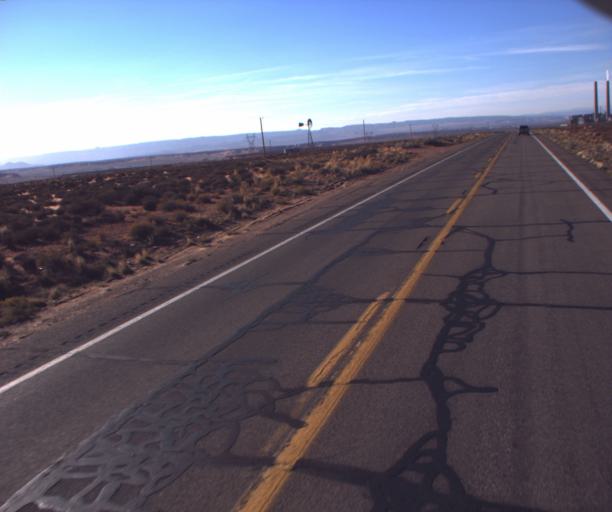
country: US
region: Arizona
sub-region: Coconino County
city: LeChee
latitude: 36.8846
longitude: -111.3571
